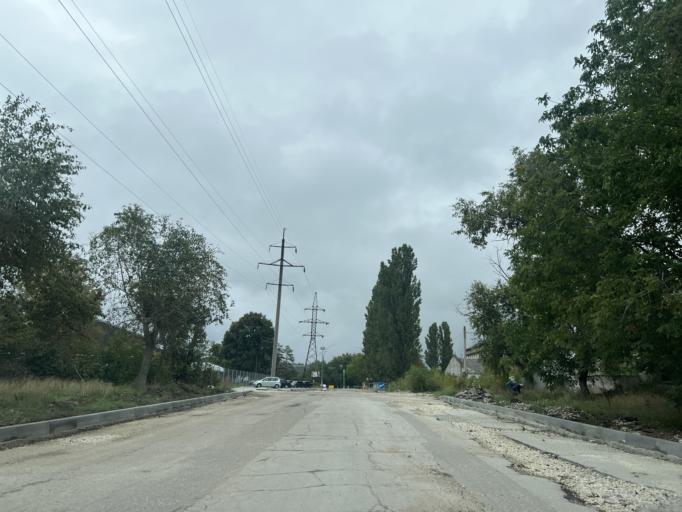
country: MD
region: Ungheni
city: Ungheni
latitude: 47.2232
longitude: 27.8079
